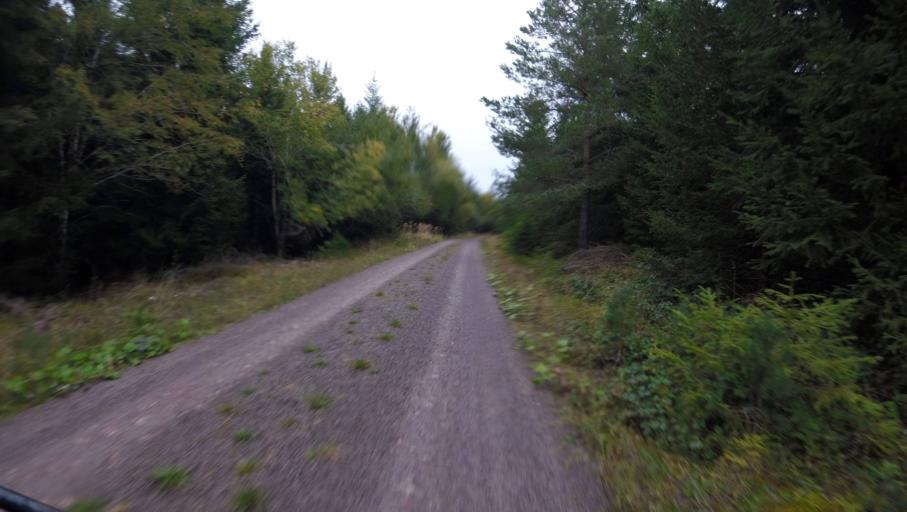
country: DE
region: Baden-Wuerttemberg
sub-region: Karlsruhe Region
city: Forbach
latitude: 48.6592
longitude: 8.4088
